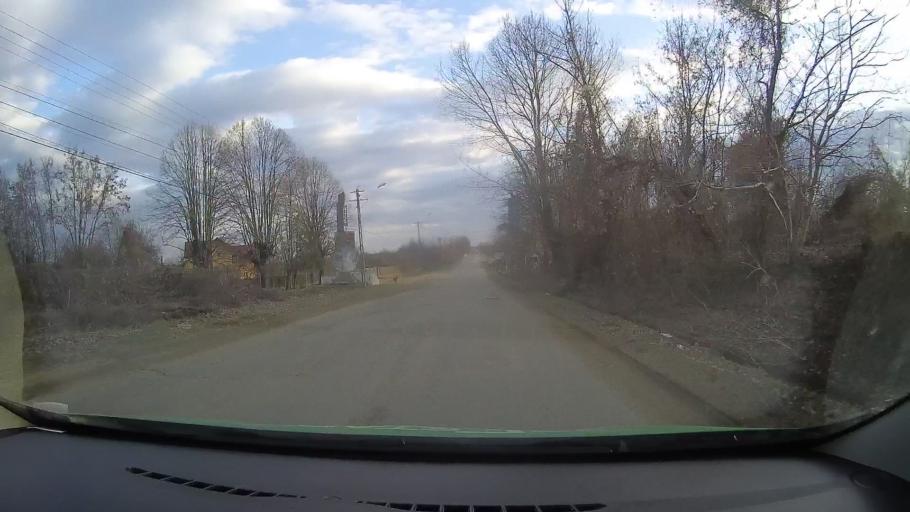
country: RO
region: Dambovita
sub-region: Municipiul Moreni
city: Moreni
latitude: 44.9612
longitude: 25.6572
